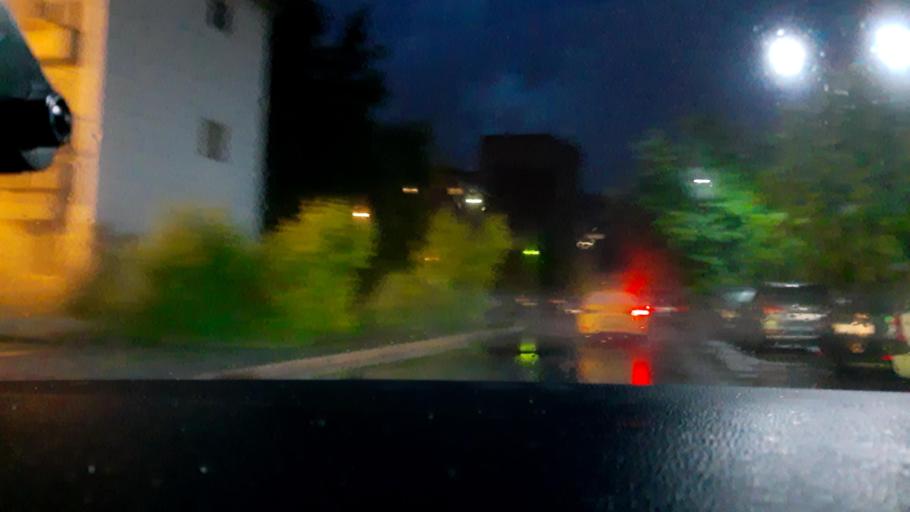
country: RU
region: Moskovskaya
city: Nakhabino
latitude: 55.8476
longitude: 37.1755
